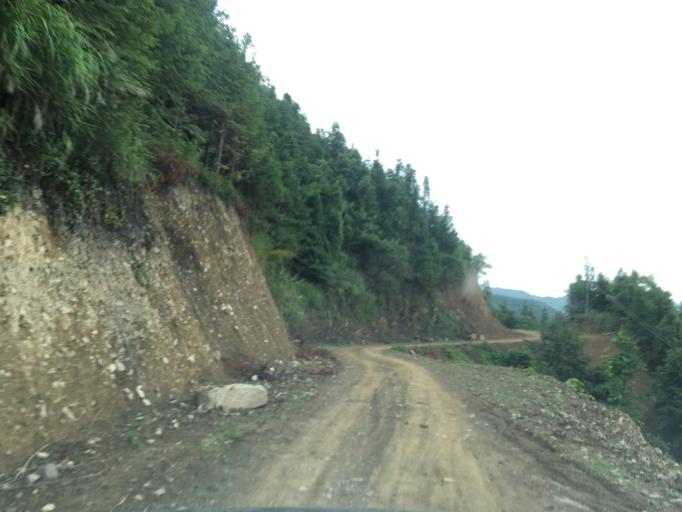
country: CN
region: Guangxi Zhuangzu Zizhiqu
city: Xinzhou
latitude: 24.8712
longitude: 105.8459
